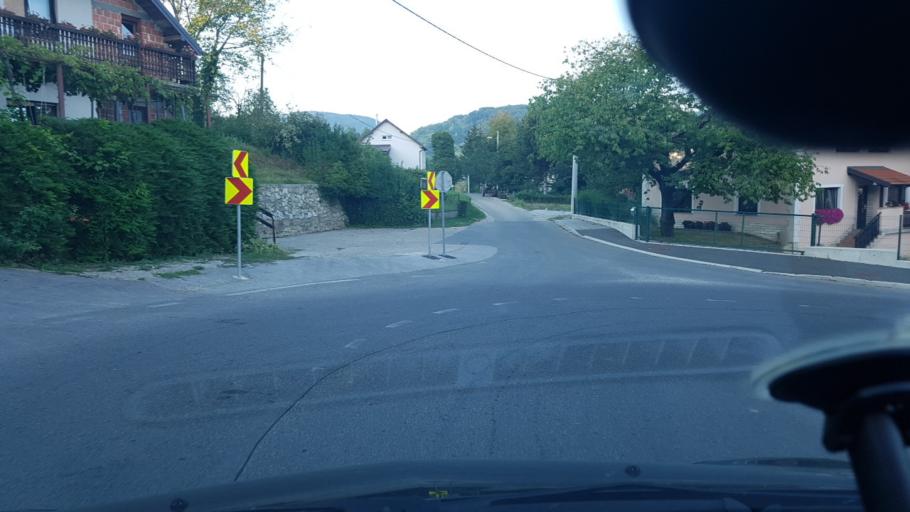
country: HR
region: Krapinsko-Zagorska
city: Pregrada
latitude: 46.1588
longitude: 15.7940
